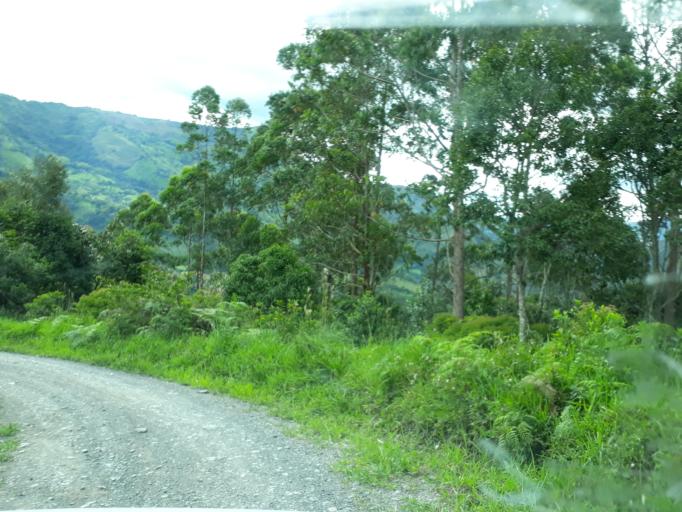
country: CO
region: Cundinamarca
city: Pacho
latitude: 5.1836
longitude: -74.2511
